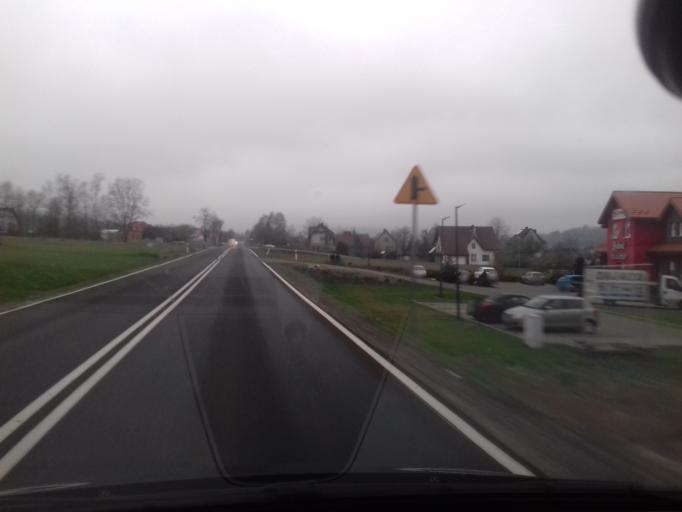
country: PL
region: Lesser Poland Voivodeship
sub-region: Powiat limanowski
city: Dobra
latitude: 49.7239
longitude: 20.2787
